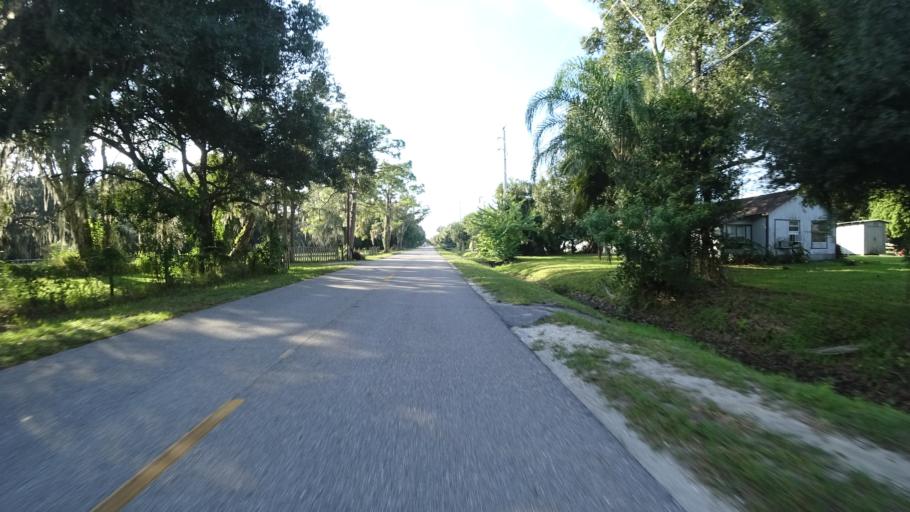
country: US
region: Florida
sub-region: Manatee County
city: Samoset
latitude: 27.4641
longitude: -82.4976
